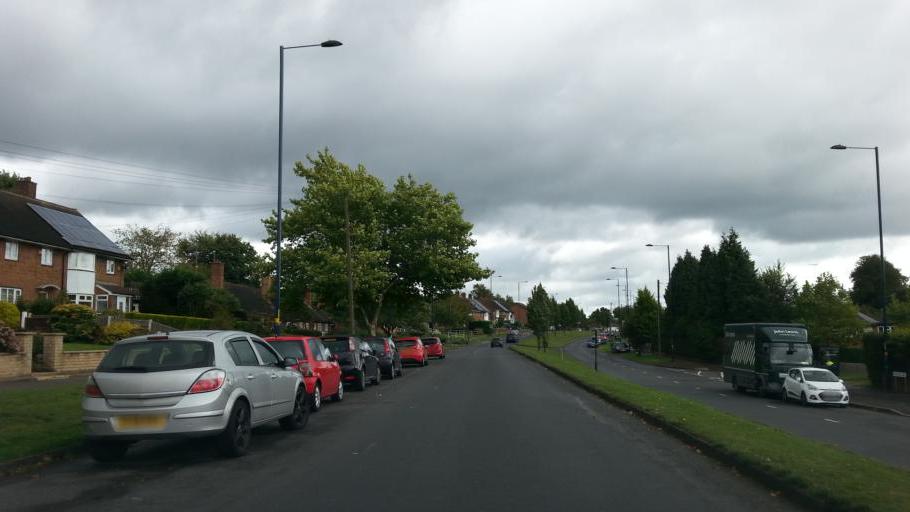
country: GB
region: England
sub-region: City and Borough of Birmingham
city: Bartley Green
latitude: 52.4607
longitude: -1.9817
